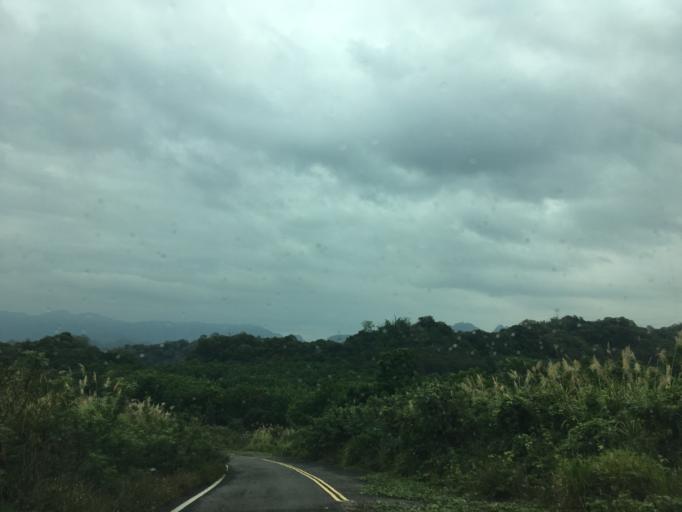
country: TW
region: Taiwan
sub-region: Taichung City
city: Taichung
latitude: 24.0569
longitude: 120.7270
